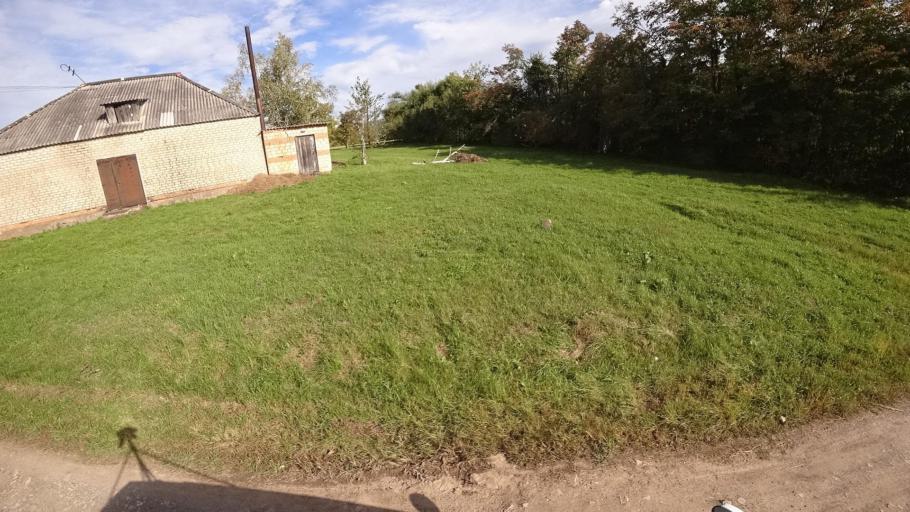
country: RU
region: Primorskiy
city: Dostoyevka
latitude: 44.2953
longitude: 133.4538
